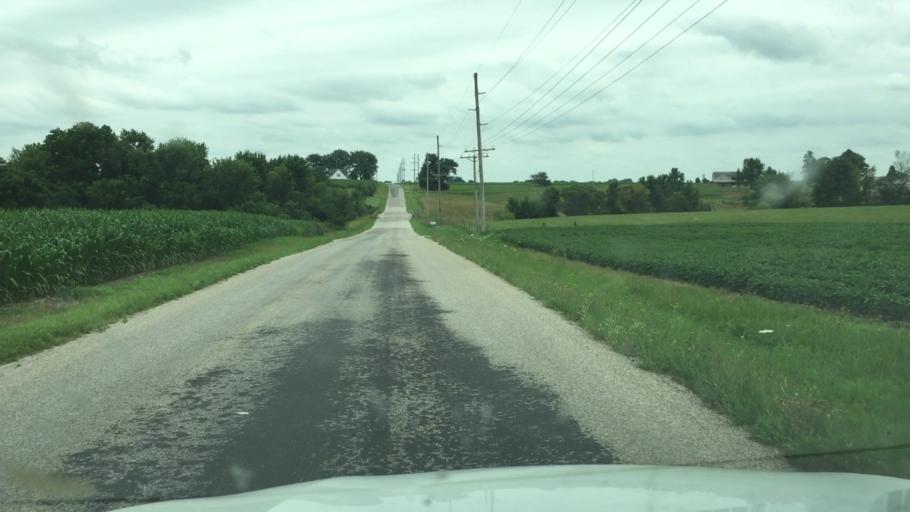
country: US
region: Illinois
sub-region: Hancock County
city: Carthage
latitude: 40.4056
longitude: -91.0824
